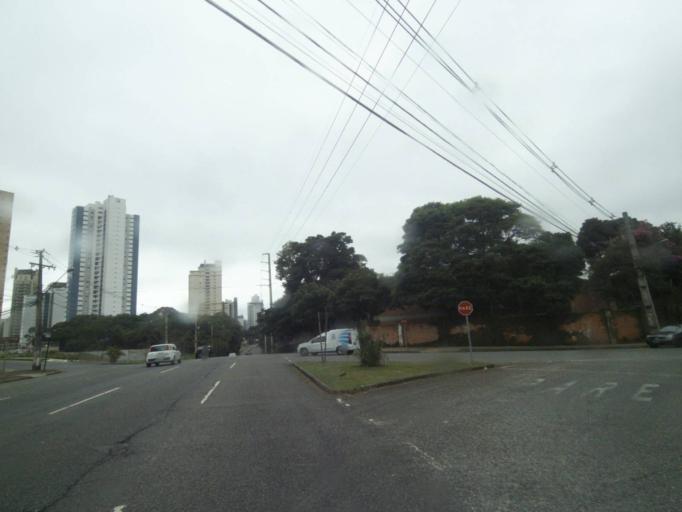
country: BR
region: Parana
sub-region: Curitiba
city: Curitiba
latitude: -25.4417
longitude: -49.3360
